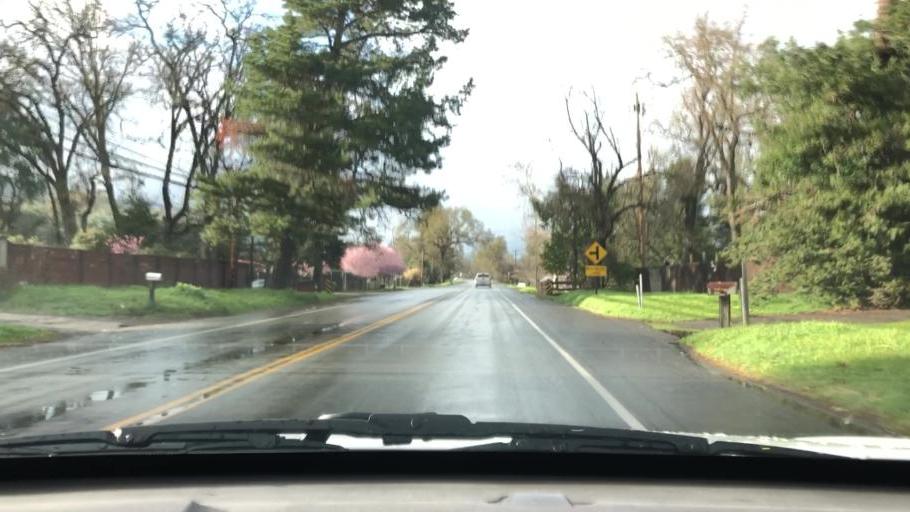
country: US
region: California
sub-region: Mendocino County
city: Talmage
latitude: 39.1133
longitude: -123.1984
